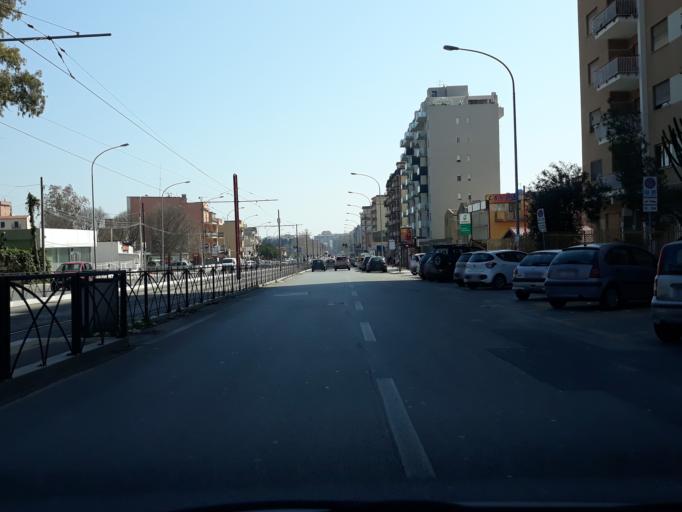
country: IT
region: Sicily
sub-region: Palermo
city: Palermo
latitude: 38.1266
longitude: 13.3104
